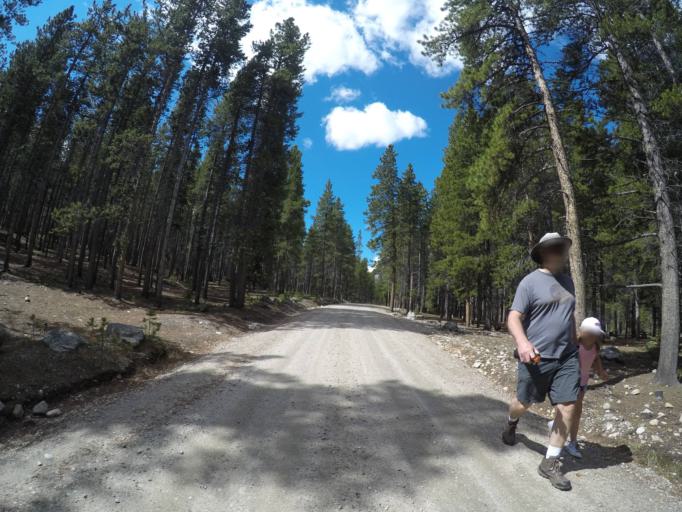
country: US
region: Montana
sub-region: Carbon County
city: Red Lodge
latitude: 45.0386
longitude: -109.4282
